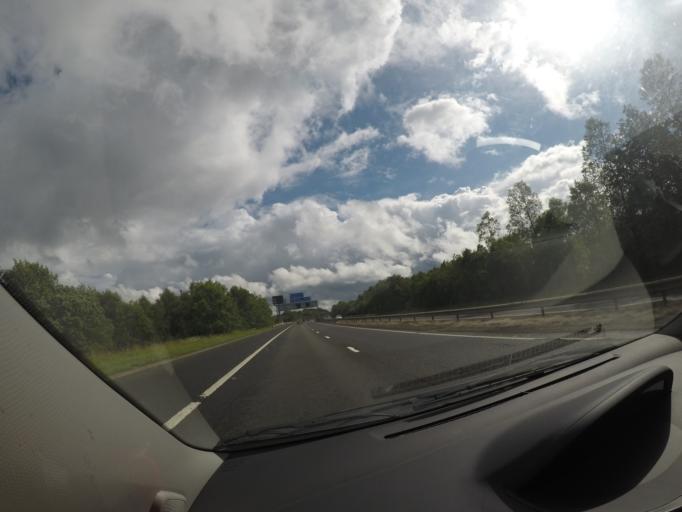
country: GB
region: Scotland
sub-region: North Lanarkshire
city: Glenboig
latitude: 55.8712
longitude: -4.0791
